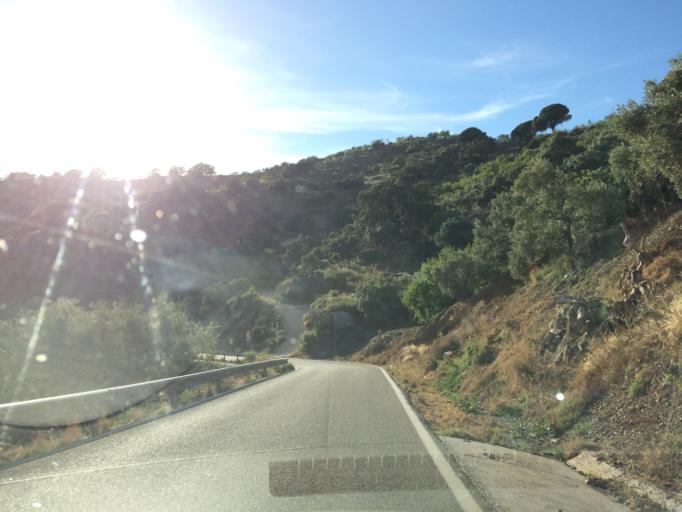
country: ES
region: Andalusia
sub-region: Provincia de Malaga
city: Totalan
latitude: 36.7780
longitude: -4.3186
